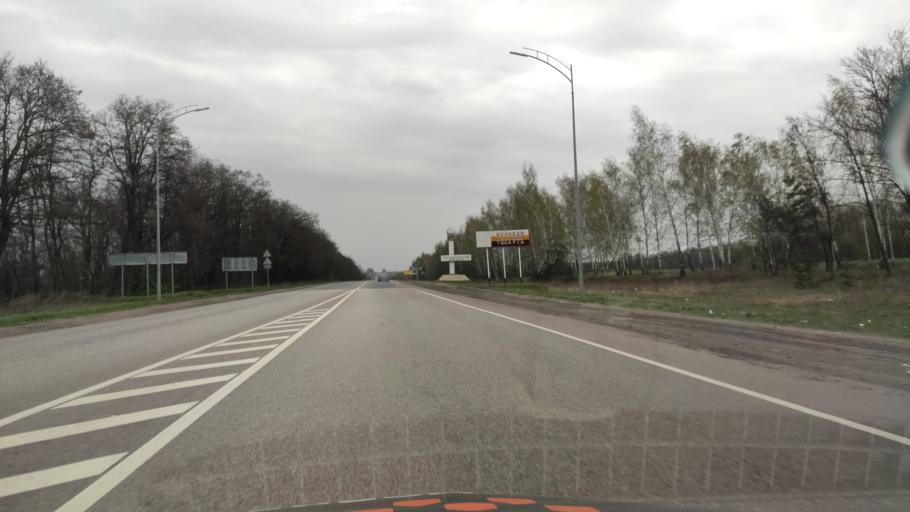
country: RU
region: Belgorod
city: Staryy Oskol
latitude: 51.4280
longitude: 37.8973
